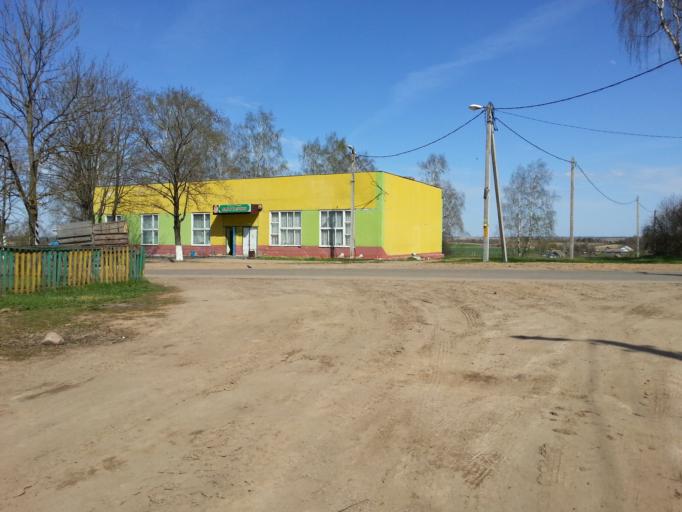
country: BY
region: Minsk
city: Khalopyenichy
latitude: 54.4319
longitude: 28.8849
